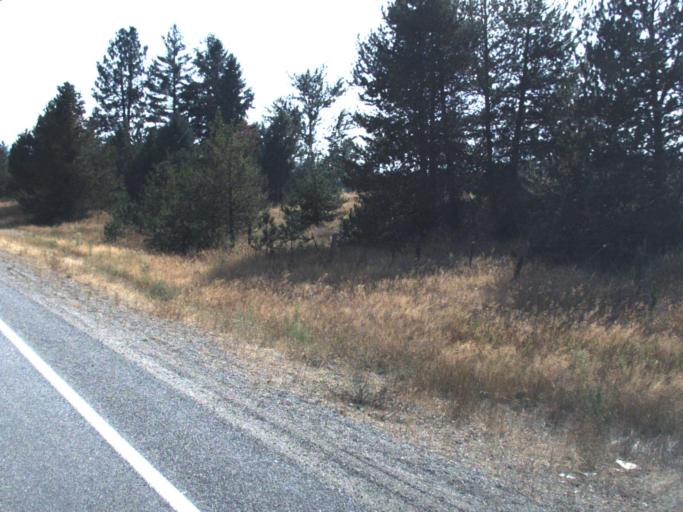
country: US
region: Washington
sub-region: Pend Oreille County
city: Newport
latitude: 48.1871
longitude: -117.3016
